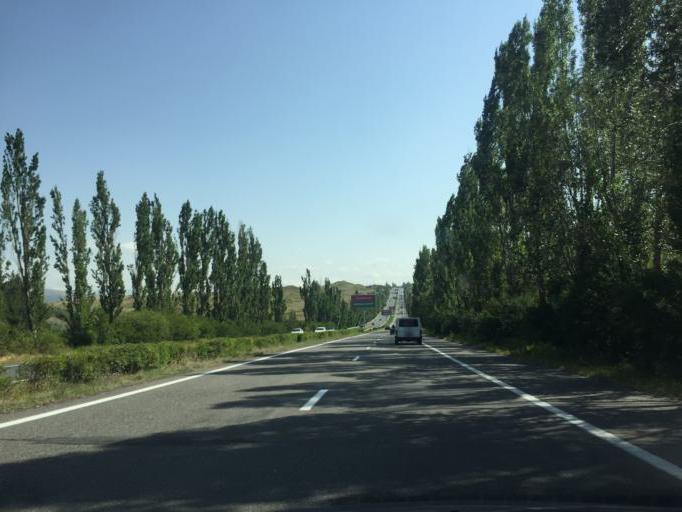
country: AM
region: Kotayk'i Marz
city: Fantan
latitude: 40.4086
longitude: 44.6821
